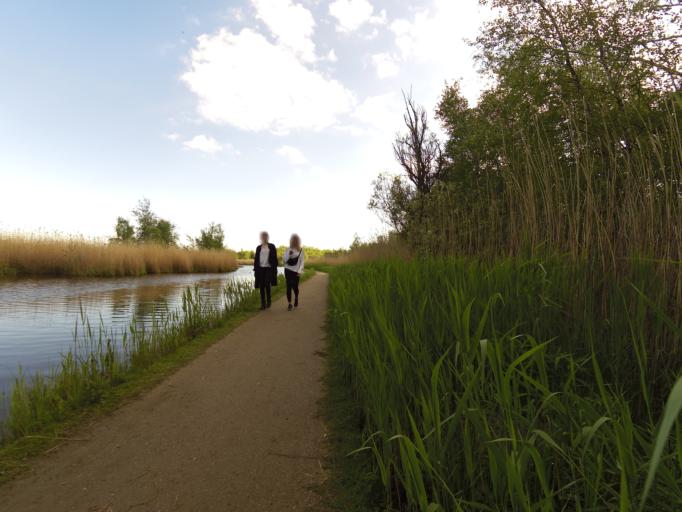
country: DK
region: Capital Region
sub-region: Lyngby-Tarbaek Kommune
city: Kongens Lyngby
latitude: 55.7492
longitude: 12.5321
